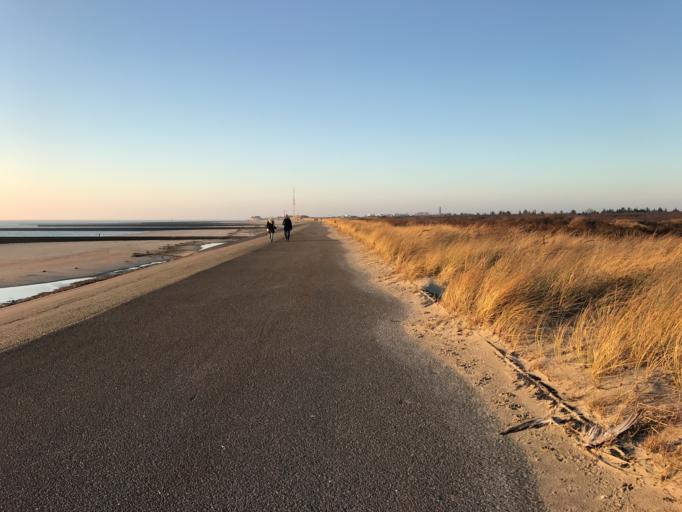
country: DE
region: Lower Saxony
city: Borkum
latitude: 53.5701
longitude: 6.6892
